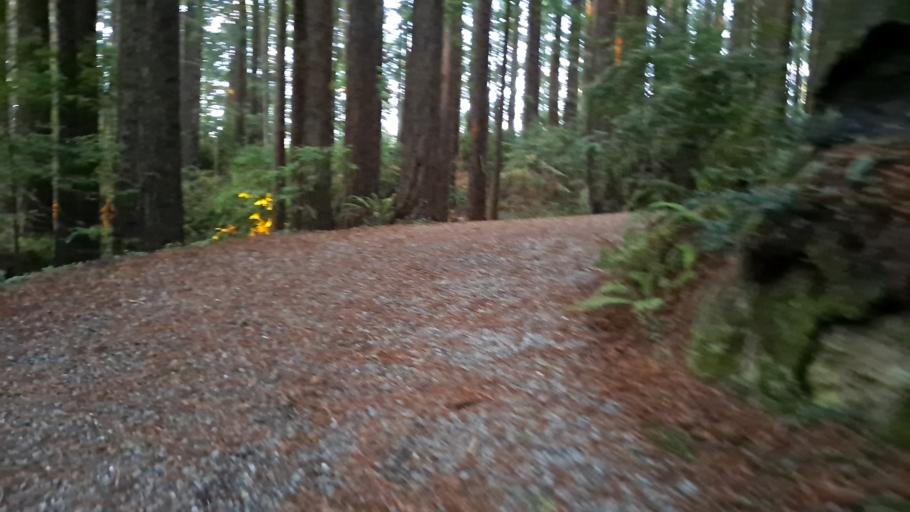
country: US
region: California
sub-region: Humboldt County
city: Fortuna
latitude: 40.6008
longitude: -124.1466
